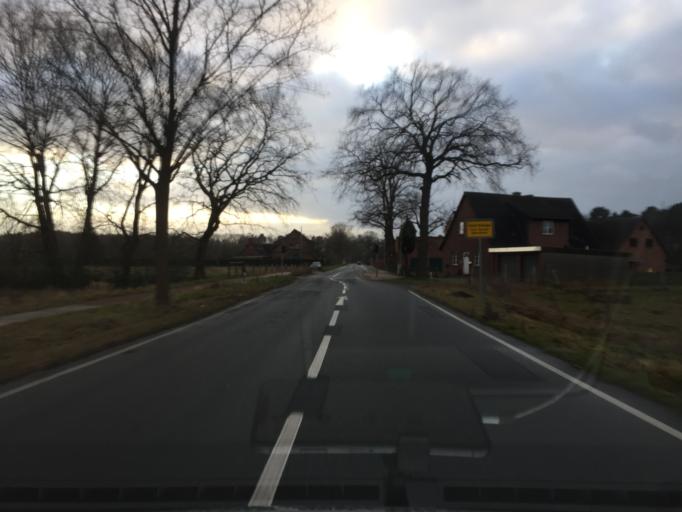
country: DE
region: Lower Saxony
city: Garbsen
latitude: 52.4358
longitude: 9.5197
